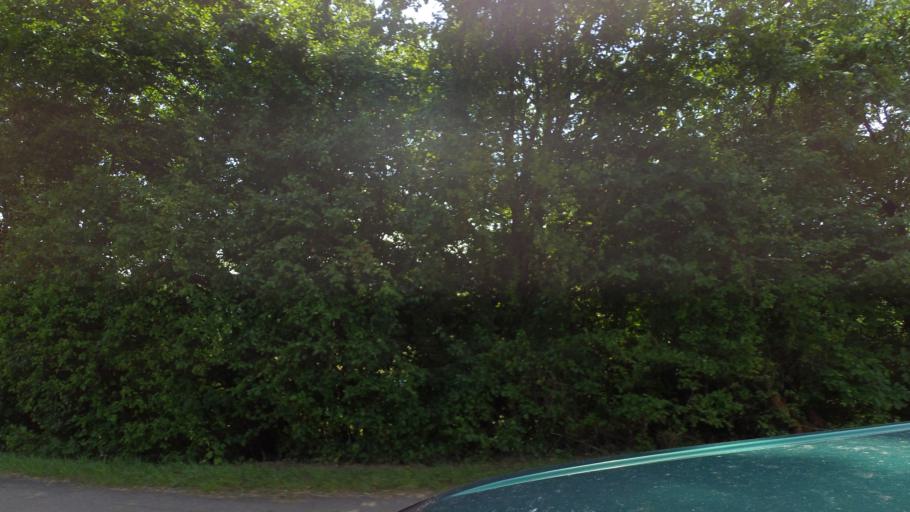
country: DE
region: Baden-Wuerttemberg
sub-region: Regierungsbezirk Stuttgart
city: Gaildorf
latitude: 48.9774
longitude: 9.8051
